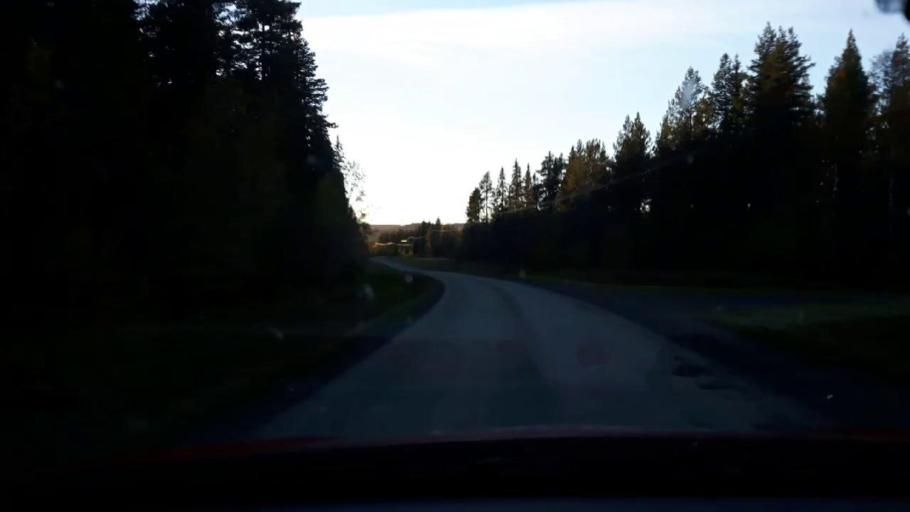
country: SE
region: Jaemtland
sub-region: Krokoms Kommun
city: Krokom
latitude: 63.4766
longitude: 14.2558
